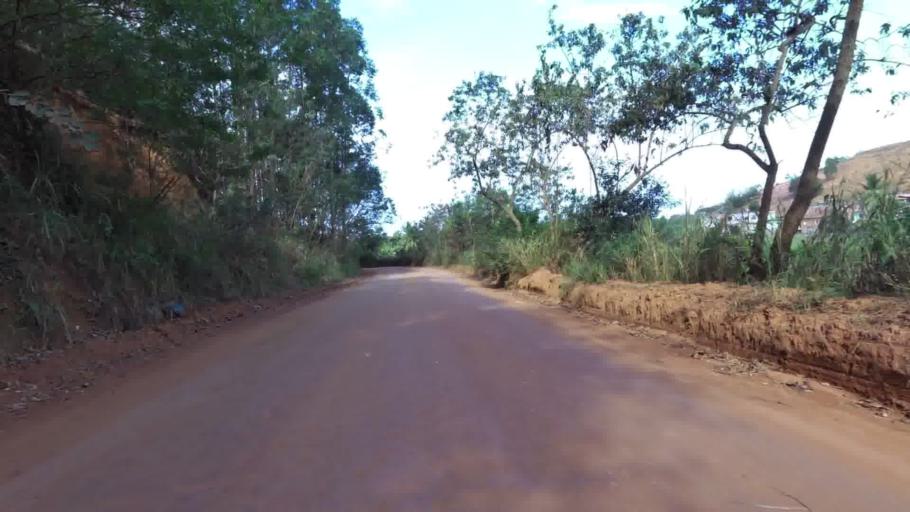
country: BR
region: Espirito Santo
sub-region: Piuma
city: Piuma
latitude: -20.8348
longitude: -40.7359
